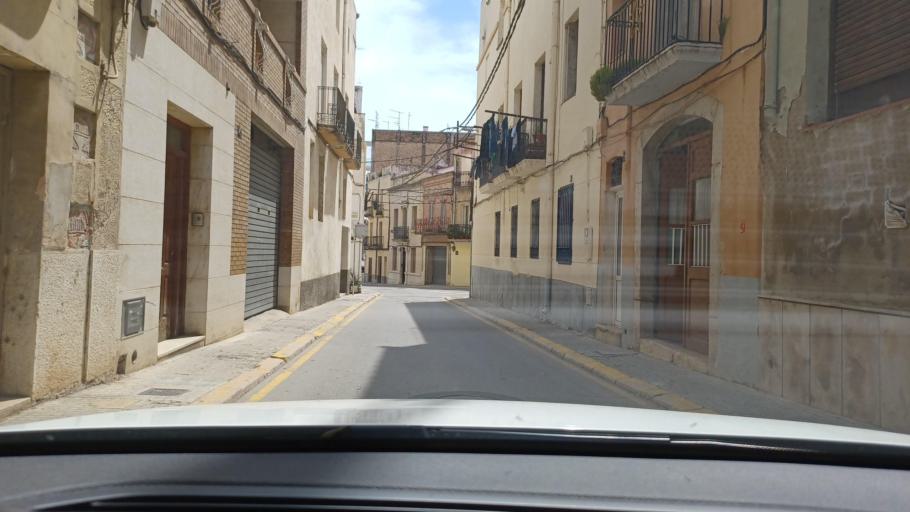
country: ES
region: Catalonia
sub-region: Provincia de Tarragona
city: Amposta
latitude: 40.7138
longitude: 0.5815
